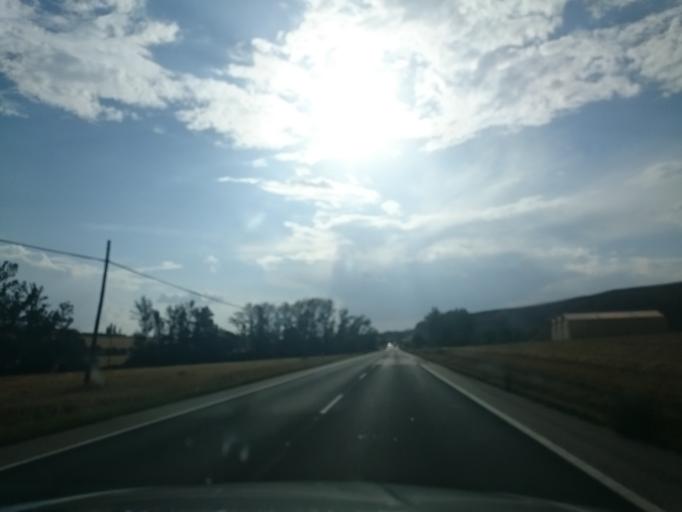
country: ES
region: Castille and Leon
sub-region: Provincia de Burgos
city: Tosantos
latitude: 42.4135
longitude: -3.2338
